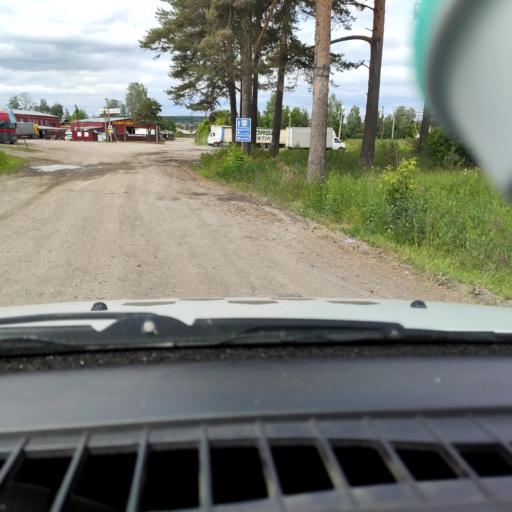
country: RU
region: Perm
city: Kondratovo
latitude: 58.0428
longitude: 56.0359
